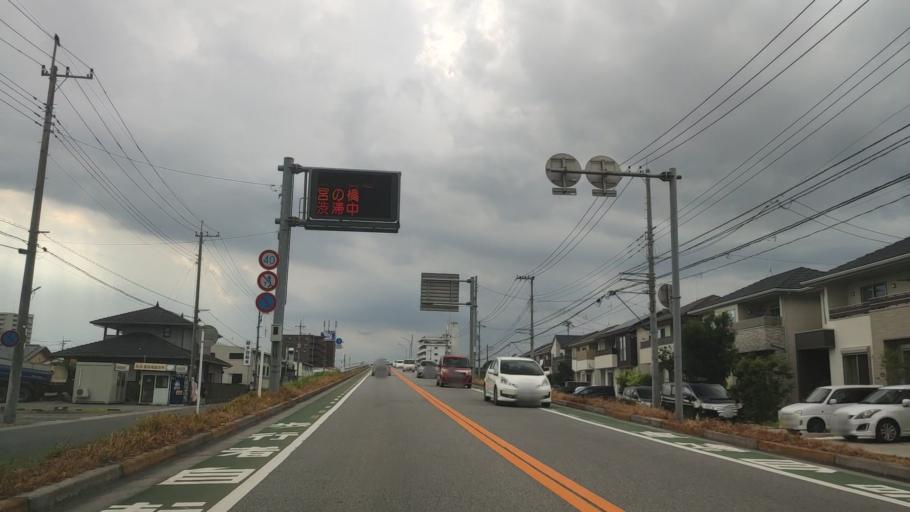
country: JP
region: Tochigi
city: Utsunomiya-shi
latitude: 36.5727
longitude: 139.9094
